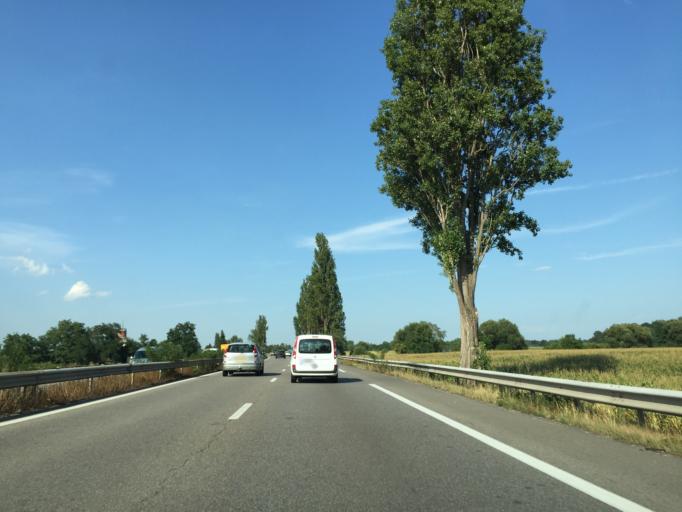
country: FR
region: Alsace
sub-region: Departement du Haut-Rhin
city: Guemar
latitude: 48.1782
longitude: 7.3820
